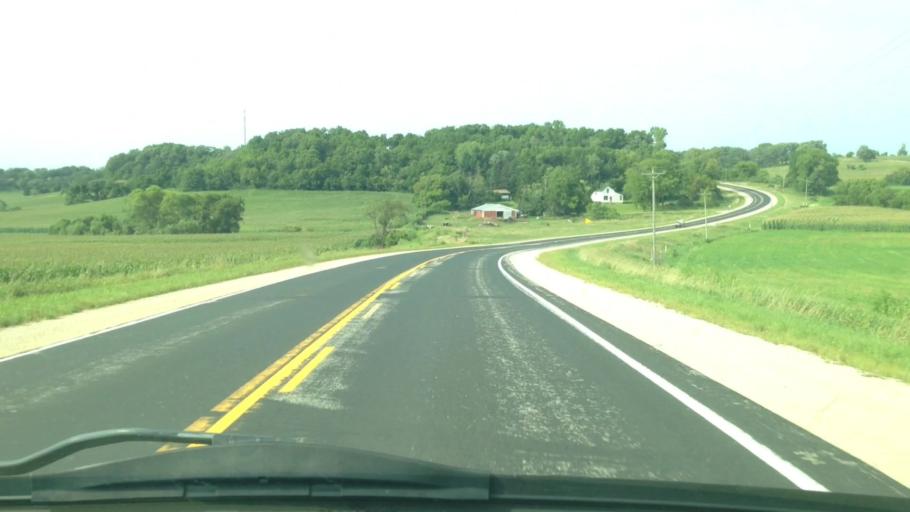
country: US
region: Minnesota
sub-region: Winona County
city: Lewiston
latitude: 43.9215
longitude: -91.9594
